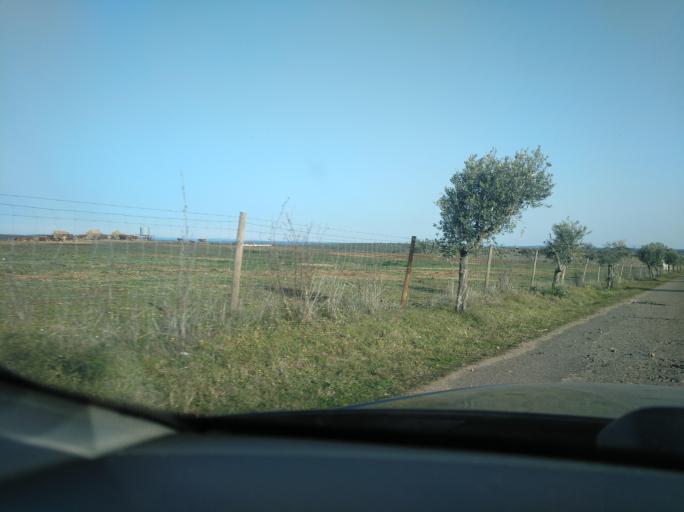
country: PT
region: Portalegre
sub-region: Campo Maior
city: Campo Maior
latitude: 39.0104
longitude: -7.0312
